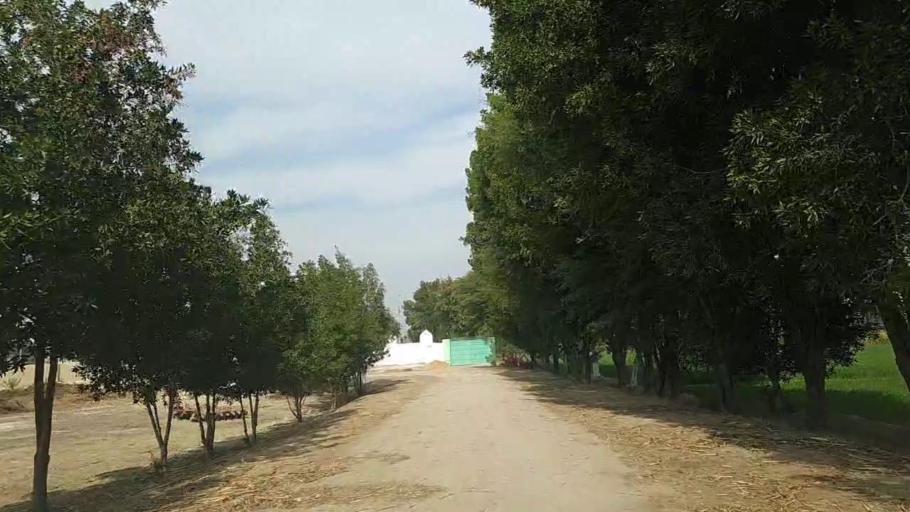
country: PK
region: Sindh
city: Daur
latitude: 26.4221
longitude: 68.4551
